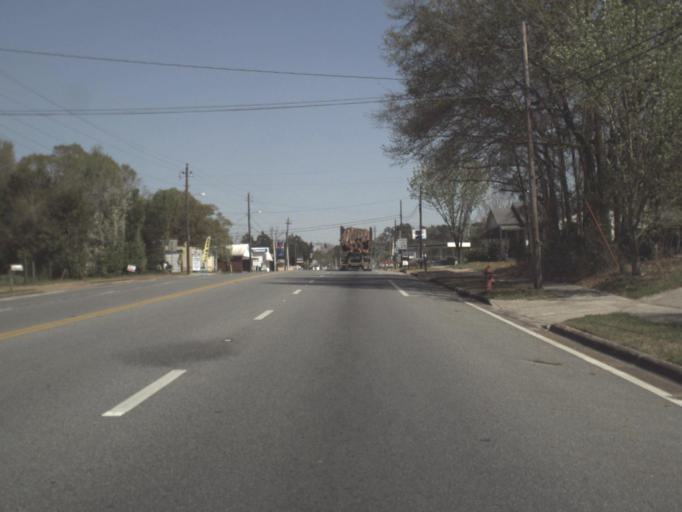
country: US
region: Florida
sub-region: Liberty County
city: Bristol
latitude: 30.4316
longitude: -84.9844
